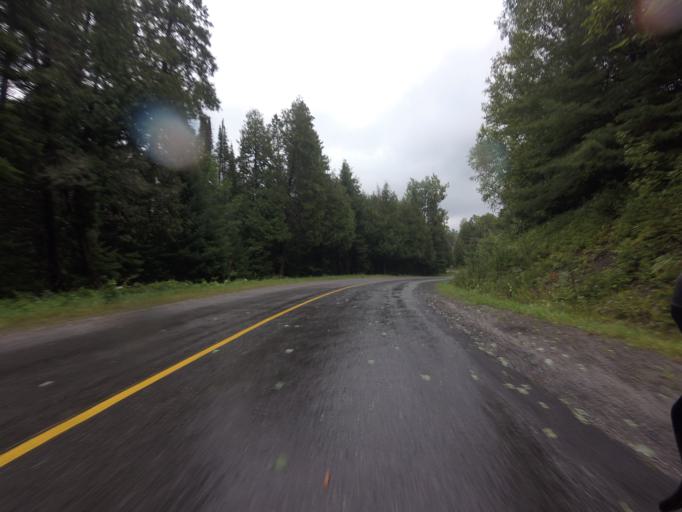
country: CA
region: Ontario
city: Perth
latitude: 45.0577
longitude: -76.5811
